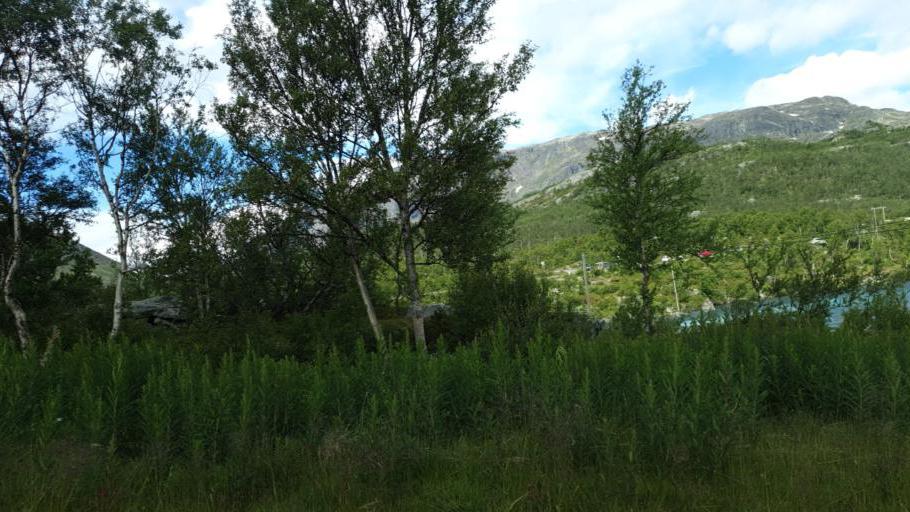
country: NO
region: Oppland
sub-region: Oystre Slidre
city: Heggenes
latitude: 61.4884
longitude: 8.8419
